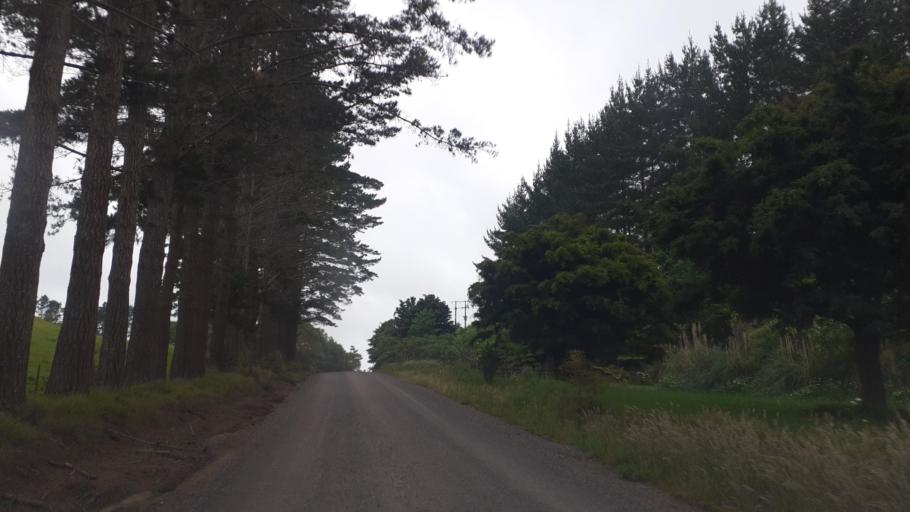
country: NZ
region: Northland
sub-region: Far North District
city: Kerikeri
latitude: -35.2799
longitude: 173.9629
